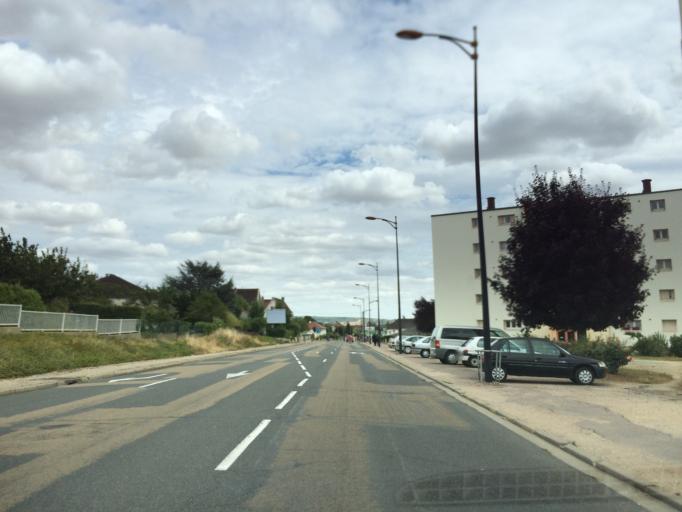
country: FR
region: Bourgogne
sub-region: Departement de l'Yonne
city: Saint-Georges-sur-Baulche
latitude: 47.7961
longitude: 3.5486
